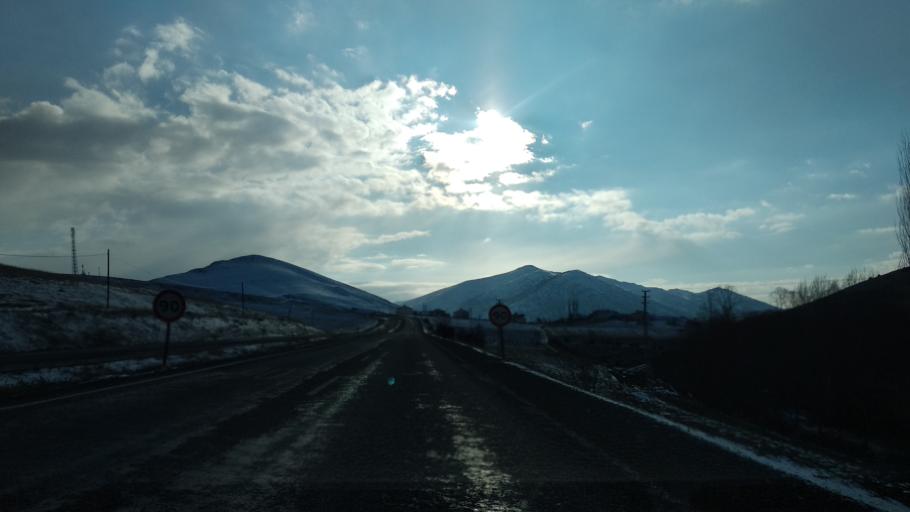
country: TR
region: Kayseri
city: Sariz
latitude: 38.3582
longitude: 36.4383
